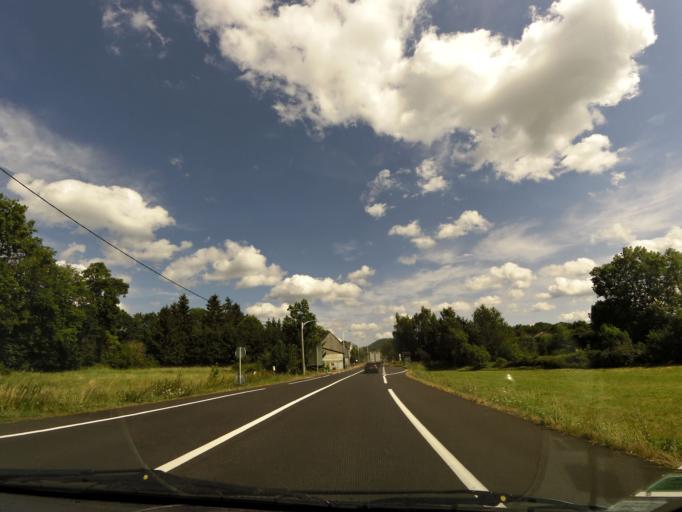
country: FR
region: Auvergne
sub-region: Departement du Puy-de-Dome
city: Aydat
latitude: 45.7275
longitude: 2.8918
